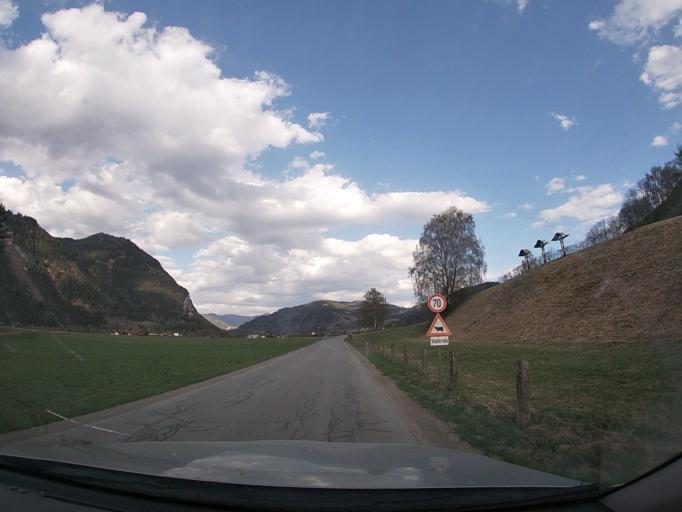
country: AT
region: Styria
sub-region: Politischer Bezirk Murau
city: Teufenbach
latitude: 47.1319
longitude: 14.3216
